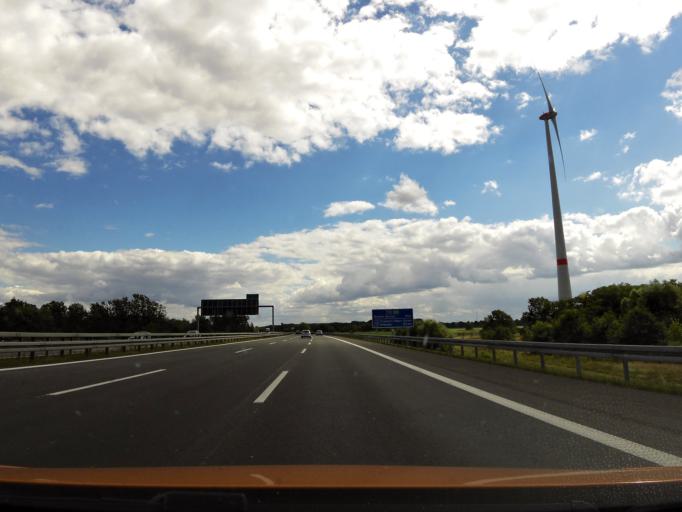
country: DE
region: Berlin
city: Buchholz
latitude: 52.6341
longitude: 13.4452
